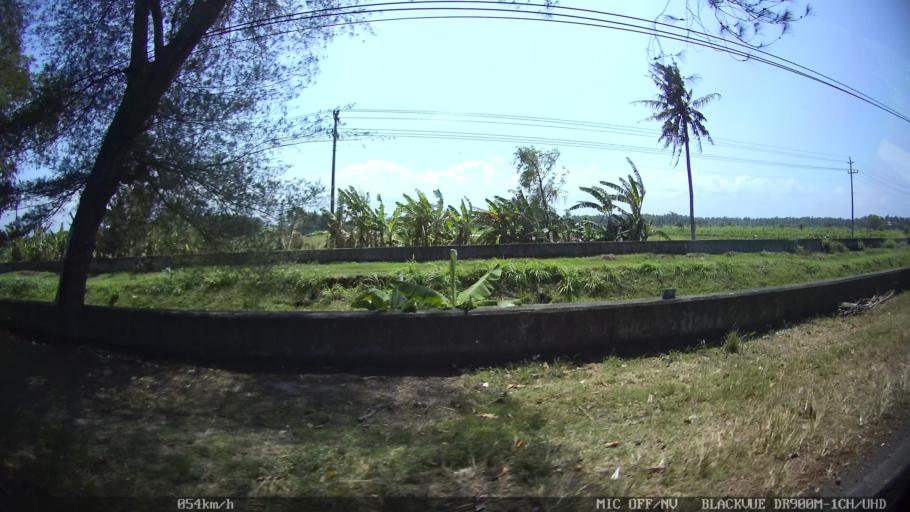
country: ID
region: Daerah Istimewa Yogyakarta
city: Srandakan
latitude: -7.9307
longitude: 110.1394
